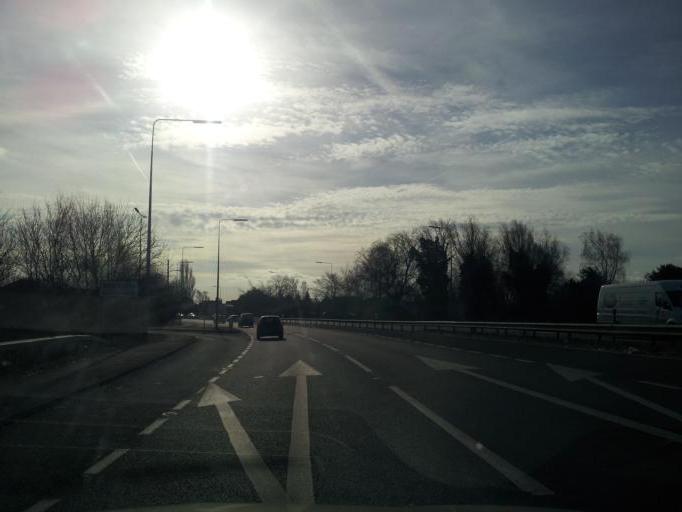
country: GB
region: England
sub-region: Central Bedfordshire
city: Sandy
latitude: 52.1226
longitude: -0.2971
